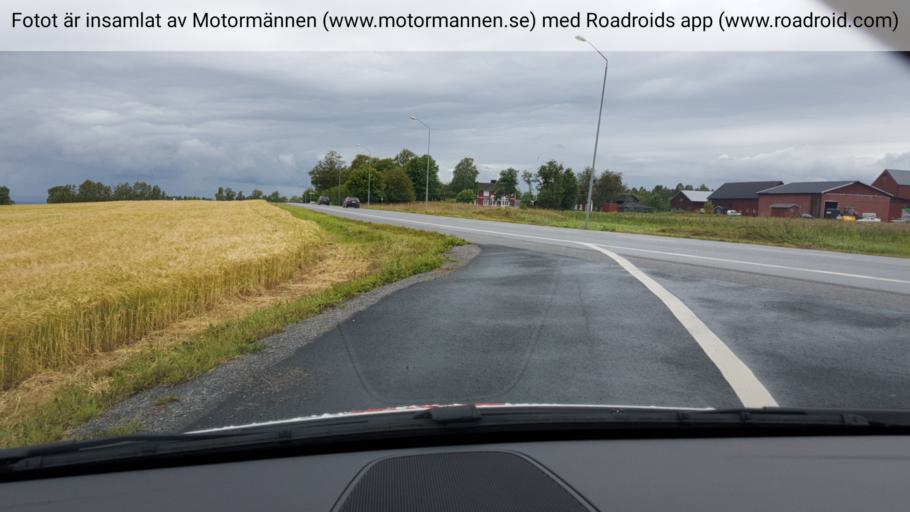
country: SE
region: Jaemtland
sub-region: OEstersunds Kommun
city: Ostersund
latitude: 63.1833
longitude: 14.5097
